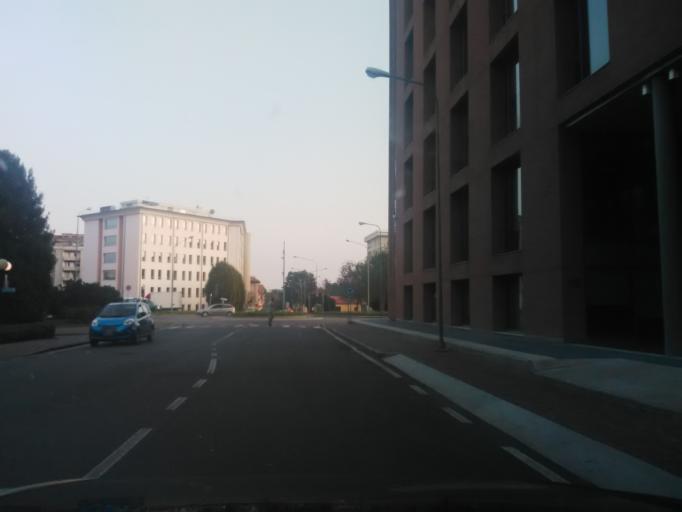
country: IT
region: Piedmont
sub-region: Provincia di Biella
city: Biella
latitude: 45.5612
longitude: 8.0551
